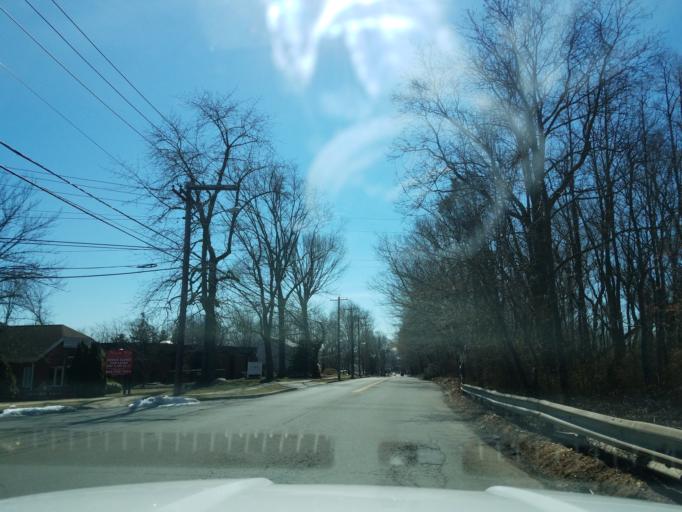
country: US
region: Connecticut
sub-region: New Haven County
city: Woodmont
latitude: 41.2461
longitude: -72.9987
